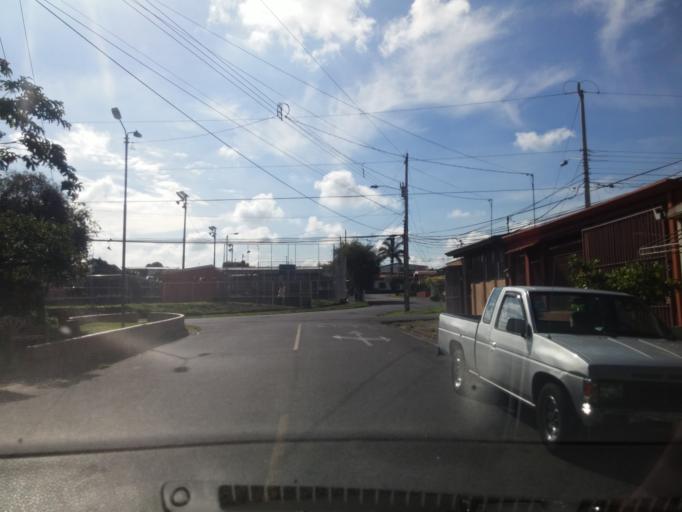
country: CR
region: Heredia
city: San Francisco
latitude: 9.9976
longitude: -84.1264
